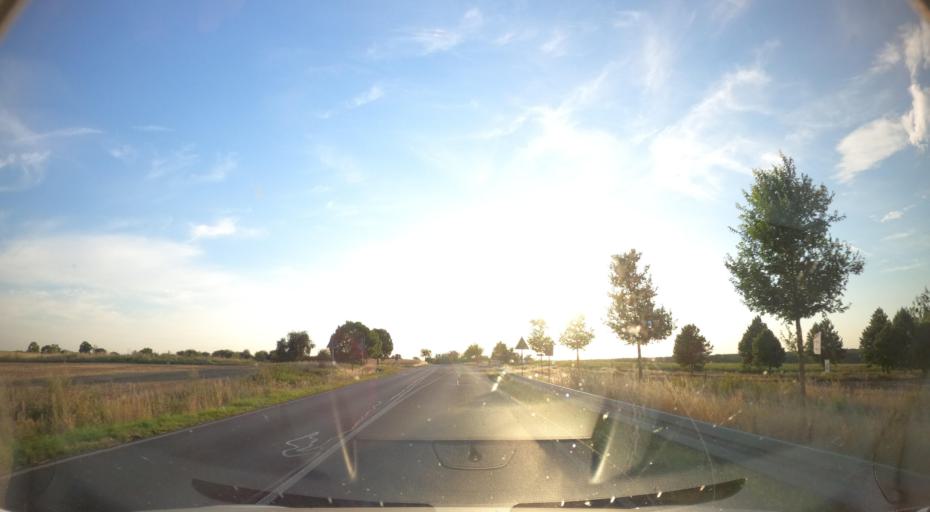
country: PL
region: West Pomeranian Voivodeship
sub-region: Powiat policki
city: Dobra
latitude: 53.4562
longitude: 14.2565
